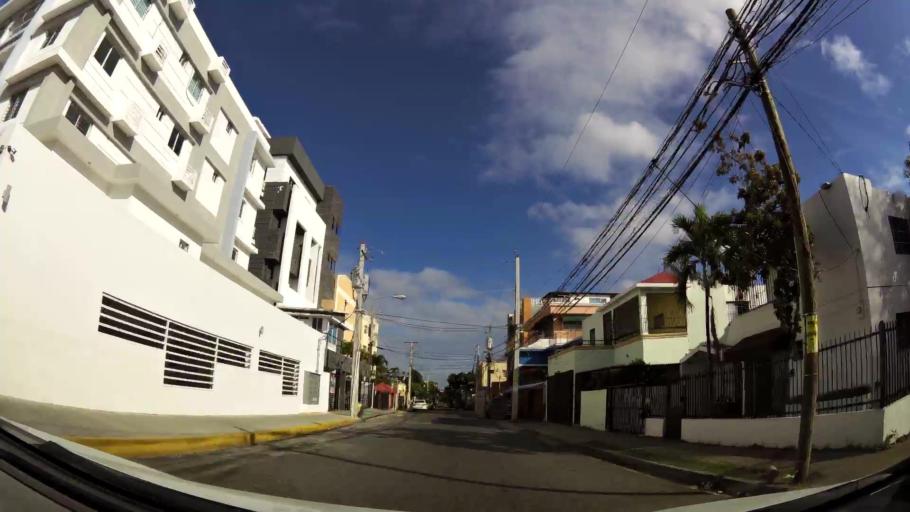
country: DO
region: Nacional
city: Bella Vista
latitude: 18.4607
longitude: -69.9509
